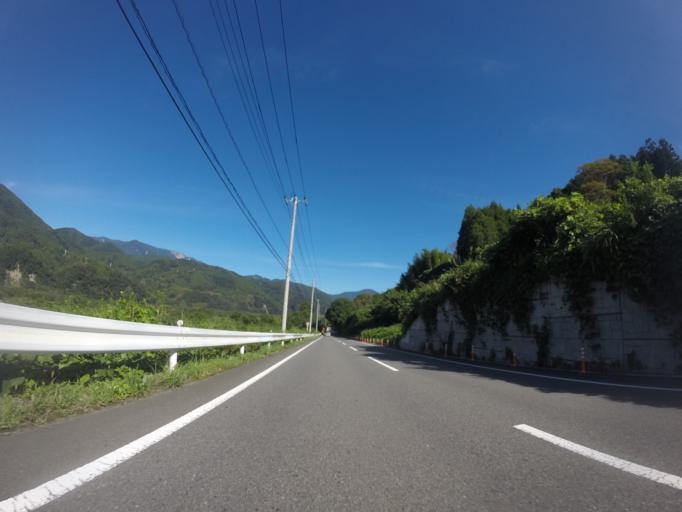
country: JP
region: Shizuoka
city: Fujinomiya
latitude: 35.3182
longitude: 138.4536
